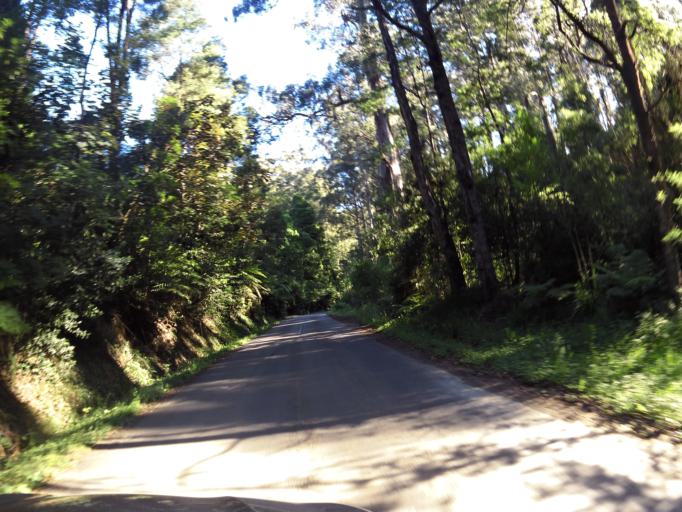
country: AU
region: Victoria
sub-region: Yarra Ranges
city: Kallista
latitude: -37.8707
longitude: 145.3616
